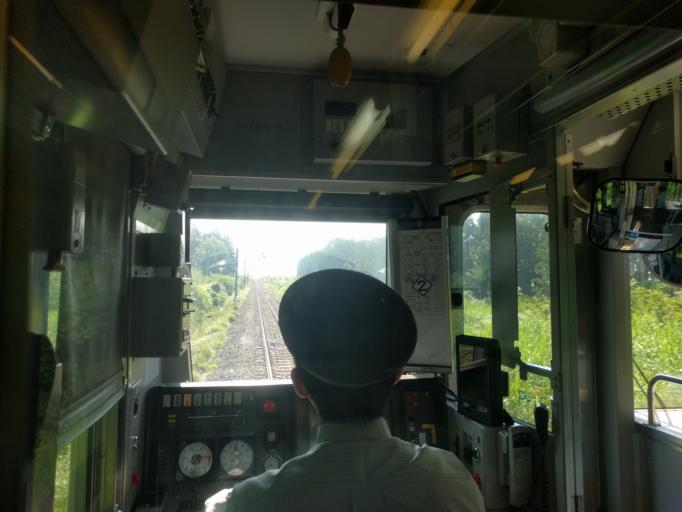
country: JP
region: Fukushima
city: Inawashiro
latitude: 37.5521
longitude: 140.0594
